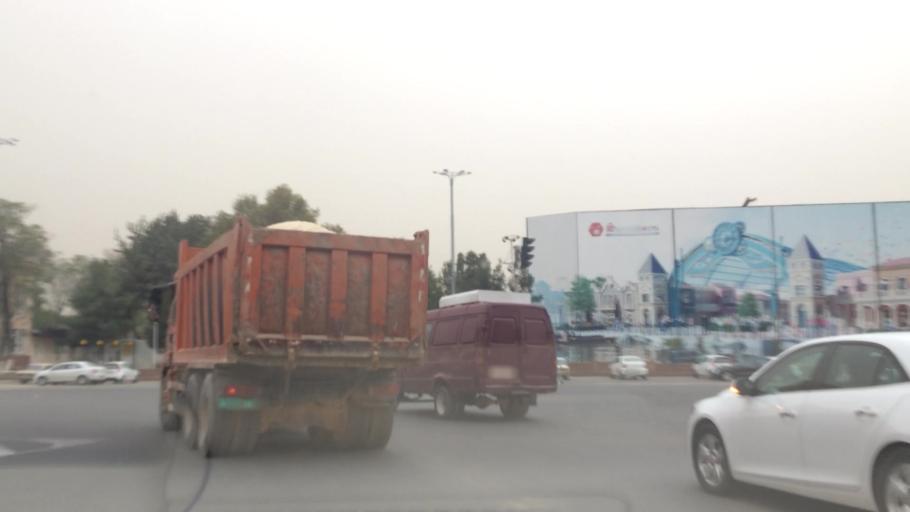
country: UZ
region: Toshkent Shahri
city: Tashkent
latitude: 41.3046
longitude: 69.2474
